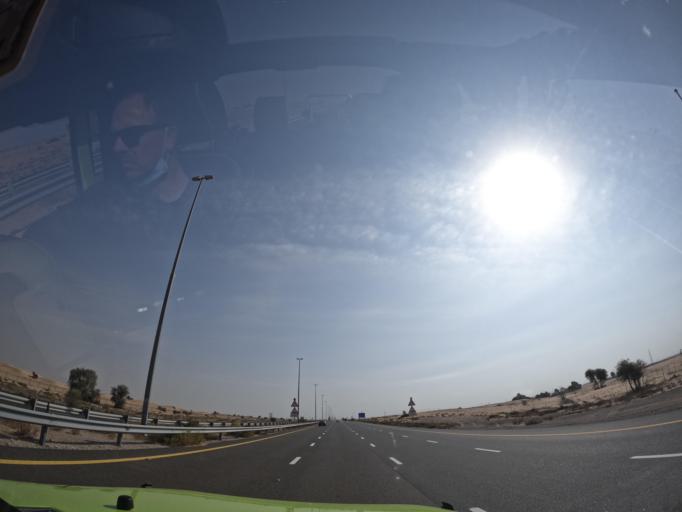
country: AE
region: Dubai
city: Dubai
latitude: 25.0098
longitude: 55.5028
